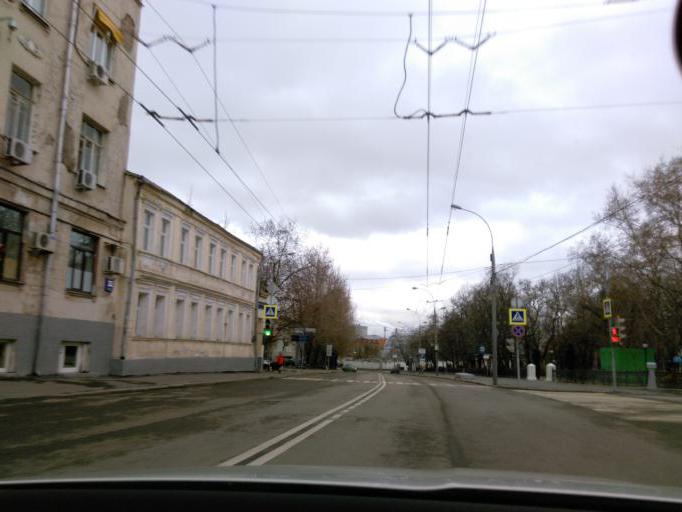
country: RU
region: Moskovskaya
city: Dorogomilovo
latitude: 55.7673
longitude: 37.5790
